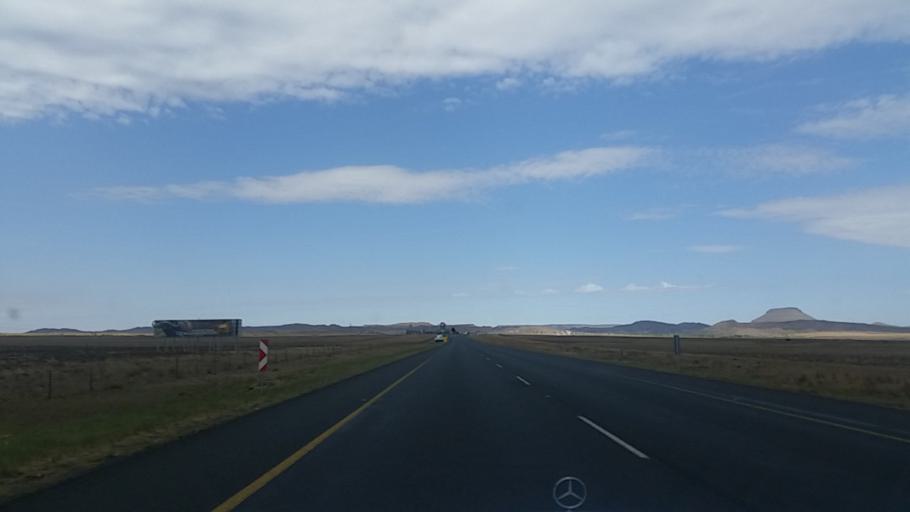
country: ZA
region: Northern Cape
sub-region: Pixley ka Seme District Municipality
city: Colesberg
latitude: -30.6816
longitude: 25.1614
